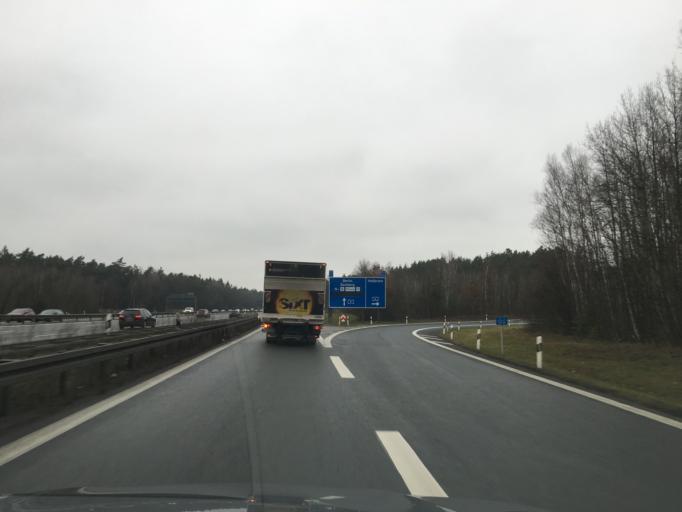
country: DE
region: Bavaria
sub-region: Regierungsbezirk Mittelfranken
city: Feucht
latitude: 49.3961
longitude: 11.2000
